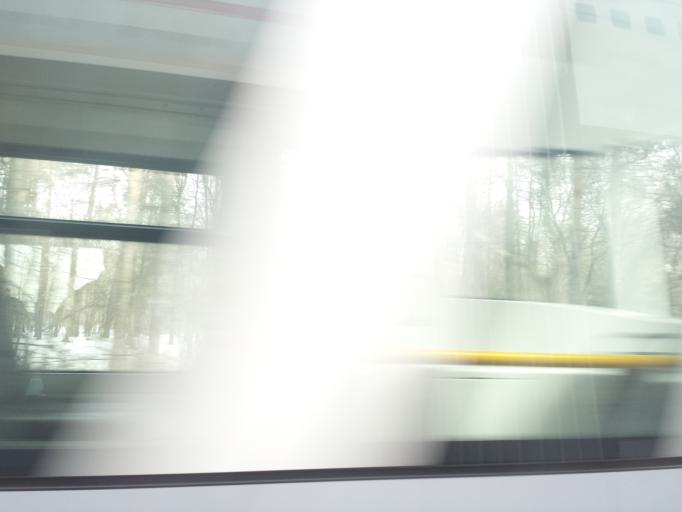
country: RU
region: Moscow
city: Pokrovskoye-Streshnevo
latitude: 55.8106
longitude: 37.4776
